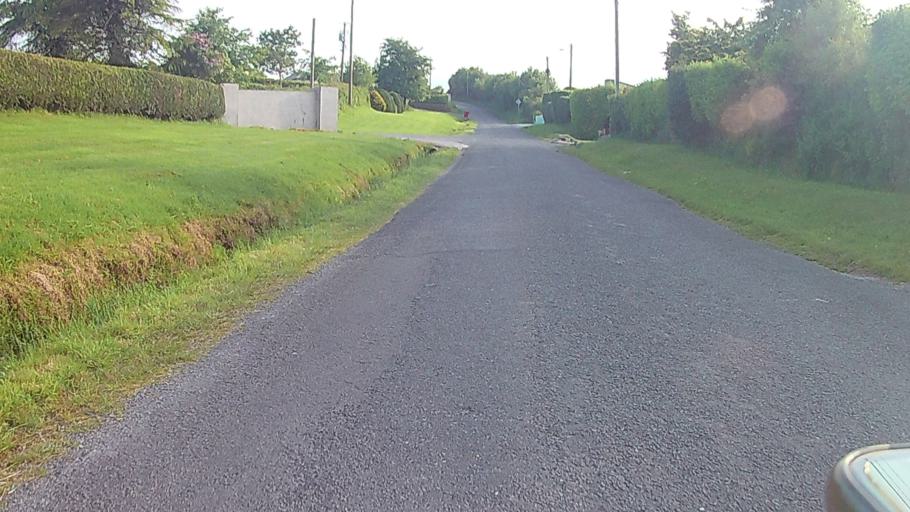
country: IE
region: Munster
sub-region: County Cork
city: Cork
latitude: 51.9724
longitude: -8.4631
